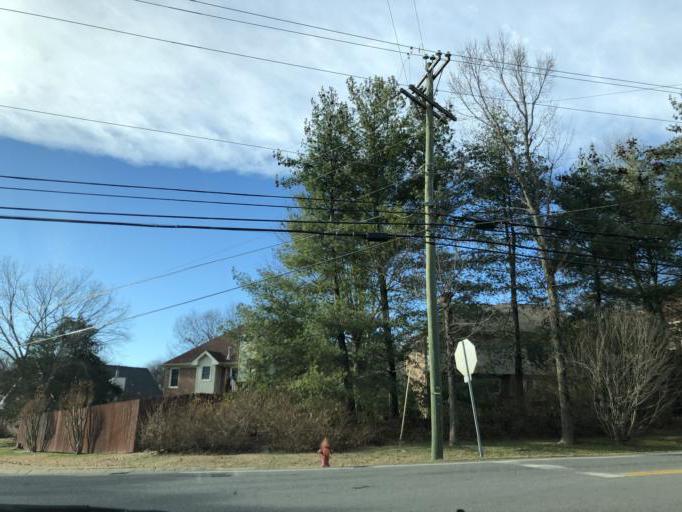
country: US
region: Tennessee
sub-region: Wilson County
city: Green Hill
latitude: 36.1549
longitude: -86.5864
